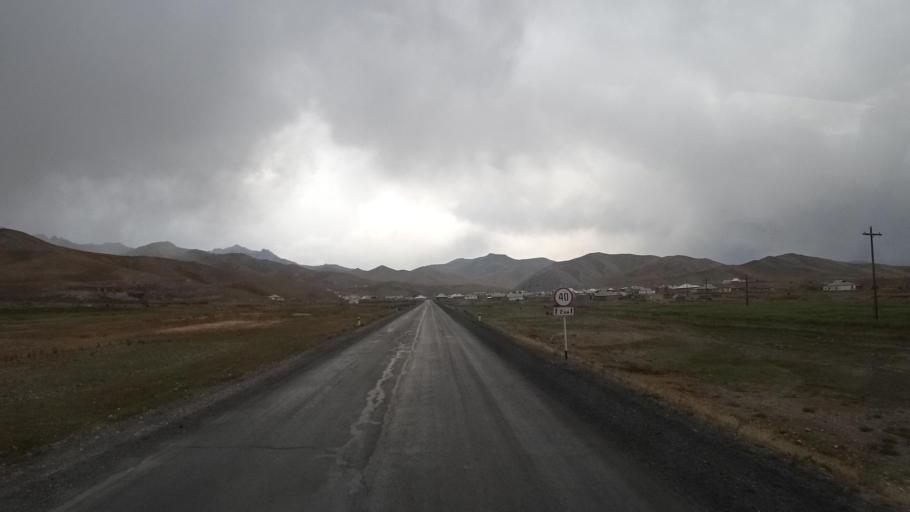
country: KG
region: Osh
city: Gul'cha
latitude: 39.7191
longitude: 73.2439
